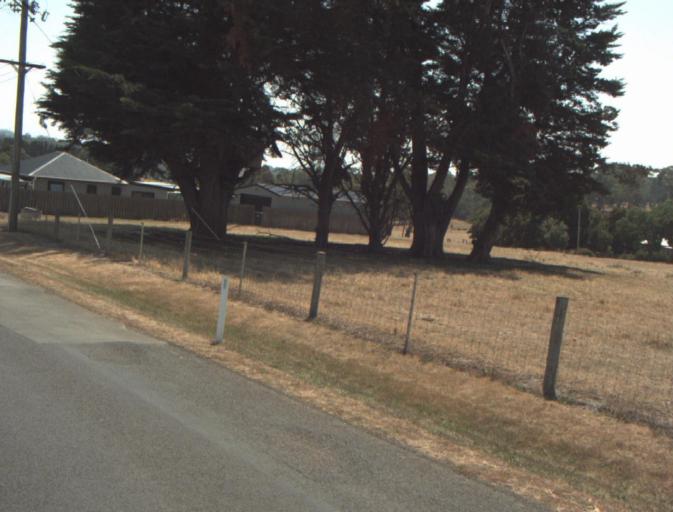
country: AU
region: Tasmania
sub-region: Northern Midlands
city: Perth
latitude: -41.5034
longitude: 147.1987
